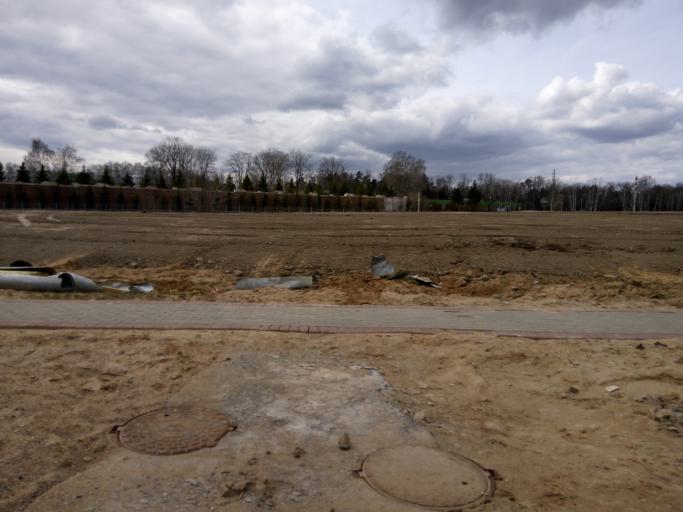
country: RU
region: Moskovskaya
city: Skolkovo
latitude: 55.6857
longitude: 37.3486
